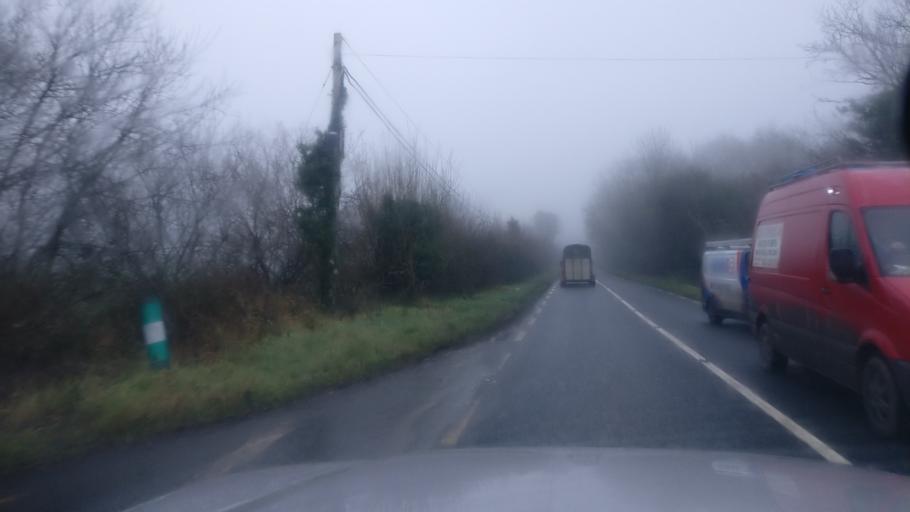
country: IE
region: Connaught
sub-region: County Galway
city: Loughrea
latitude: 53.1667
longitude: -8.6751
